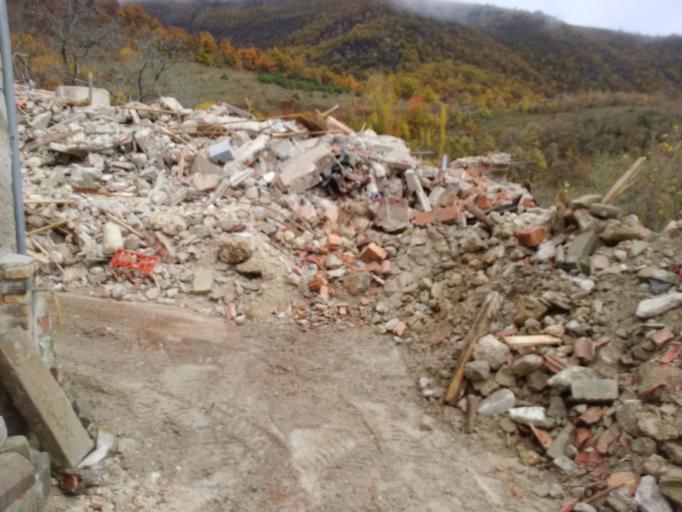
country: IT
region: Latium
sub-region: Provincia di Rieti
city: Accumoli
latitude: 42.6929
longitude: 13.2081
